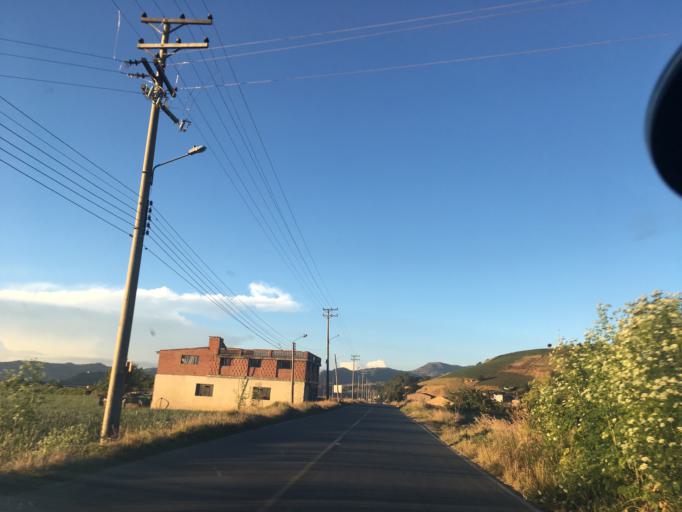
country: CO
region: Boyaca
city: Aquitania
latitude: 5.5304
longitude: -72.8841
